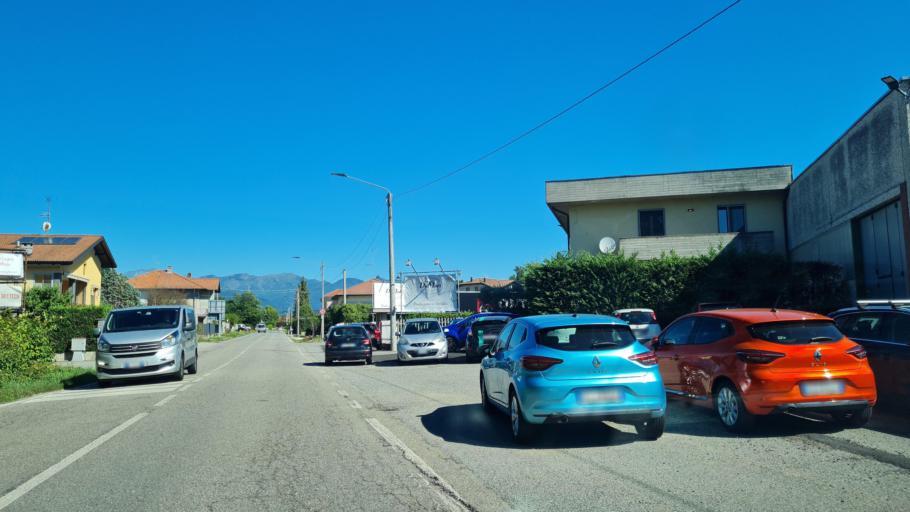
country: IT
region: Piedmont
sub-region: Provincia di Biella
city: Cossato
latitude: 45.5537
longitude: 8.2061
